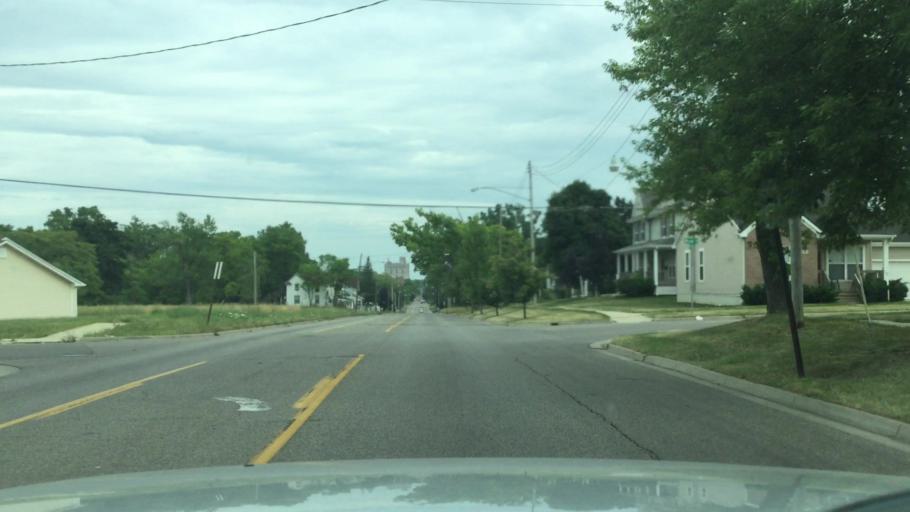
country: US
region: Michigan
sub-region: Genesee County
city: Flint
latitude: 43.0295
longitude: -83.7023
